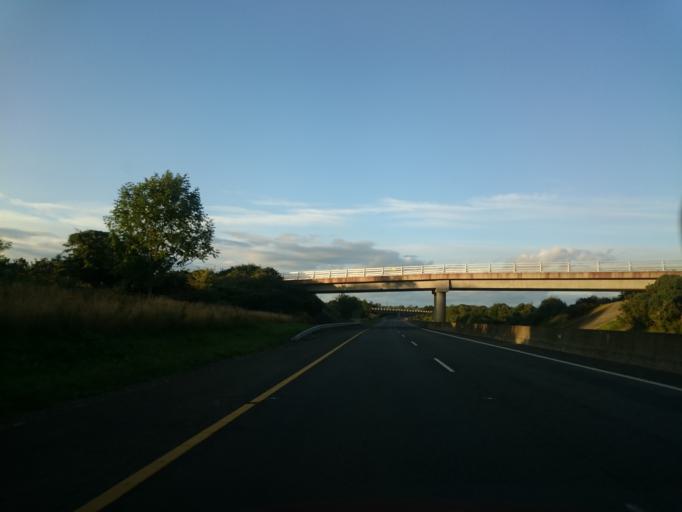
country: IE
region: Leinster
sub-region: Loch Garman
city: Gorey
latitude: 52.6386
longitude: -6.3427
